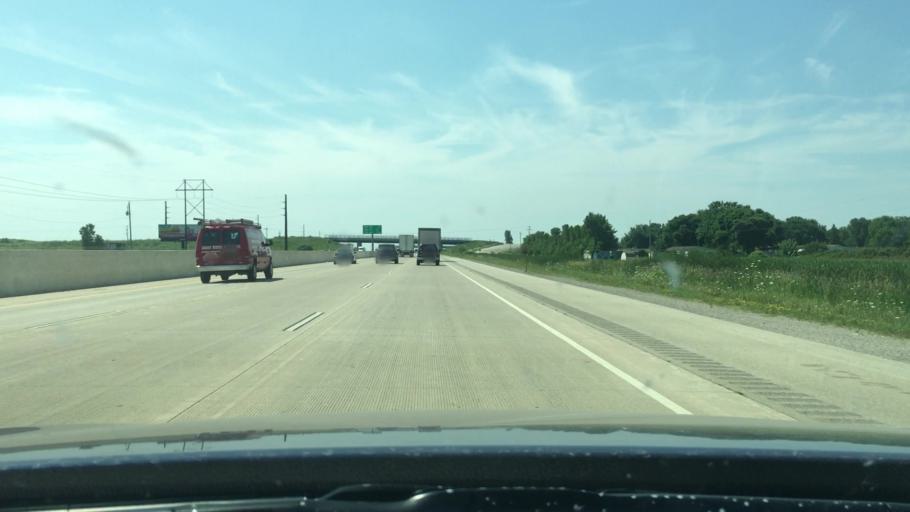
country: US
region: Wisconsin
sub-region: Winnebago County
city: Oshkosh
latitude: 44.0723
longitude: -88.5668
